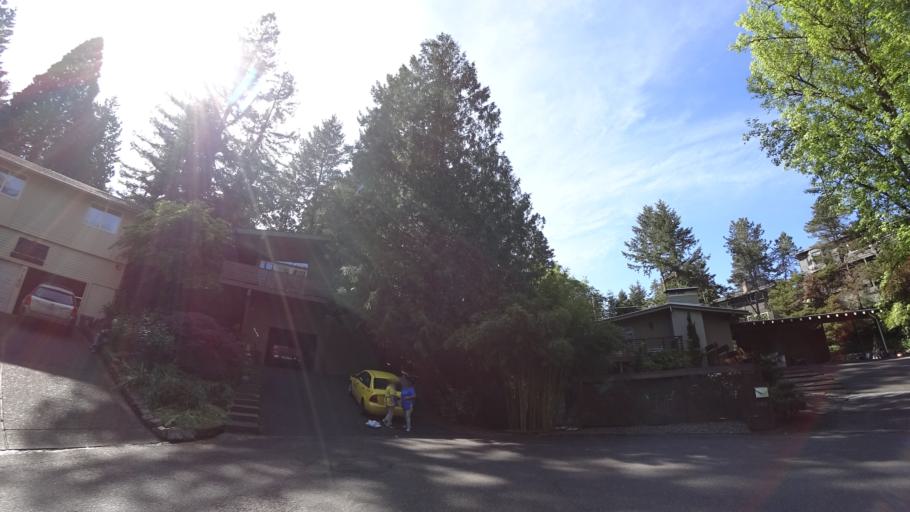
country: US
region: Oregon
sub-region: Washington County
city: West Slope
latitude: 45.4933
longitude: -122.7503
